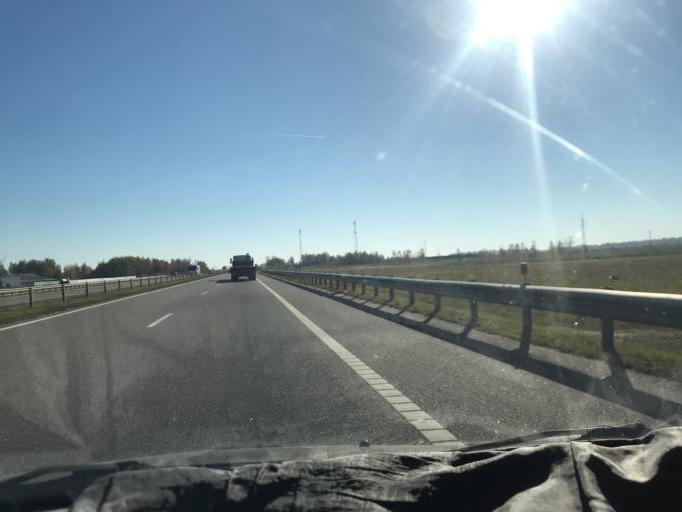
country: BY
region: Mogilev
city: Yalizava
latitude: 53.2523
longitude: 28.9200
